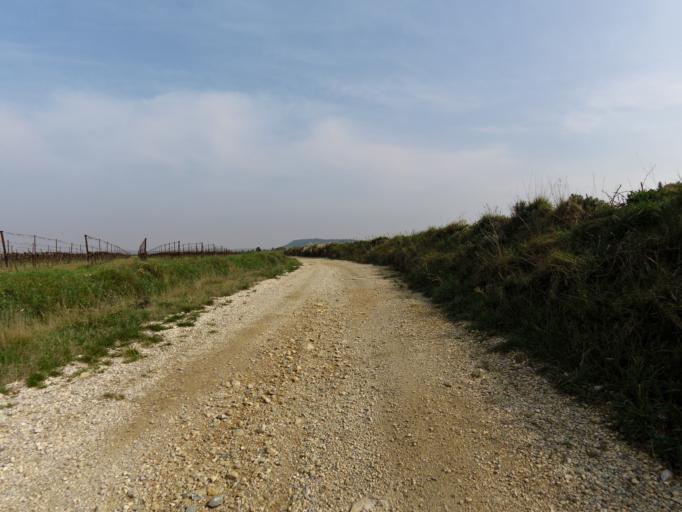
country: FR
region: Languedoc-Roussillon
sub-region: Departement du Gard
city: Calvisson
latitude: 43.7687
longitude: 4.2054
